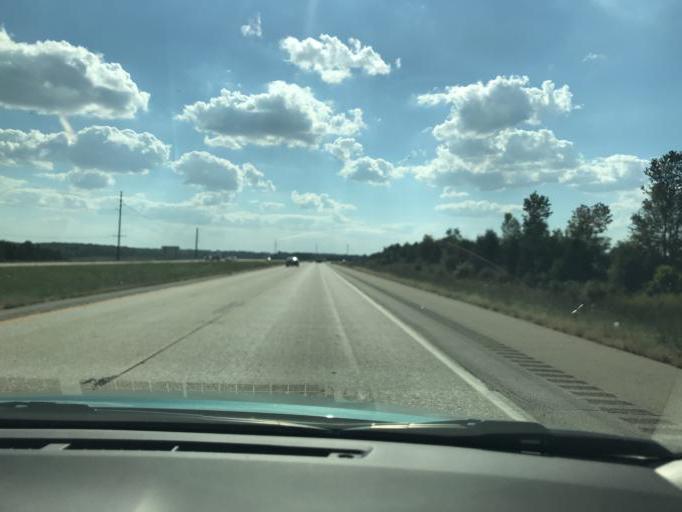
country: US
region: Wisconsin
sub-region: Walworth County
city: Delavan
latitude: 42.6168
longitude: -88.6340
